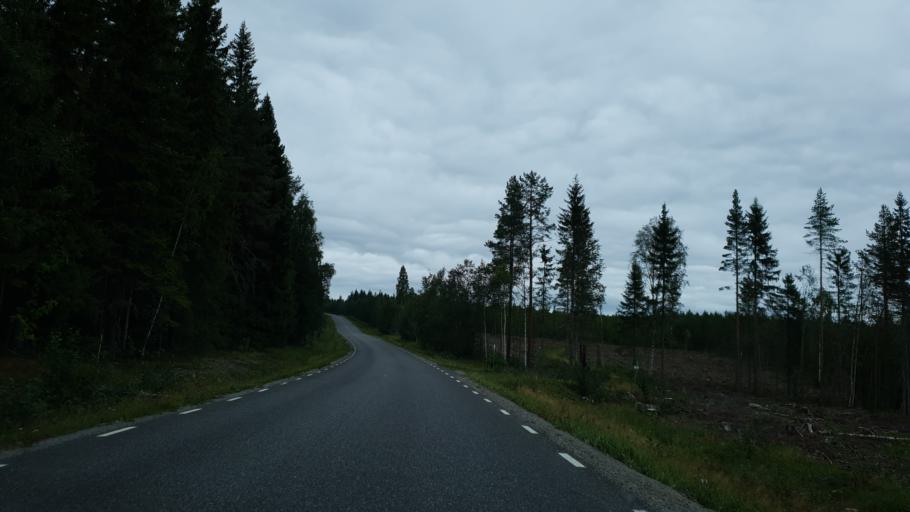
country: SE
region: Vaesterbotten
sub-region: Skelleftea Kommun
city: Viken
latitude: 64.8010
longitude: 20.7453
